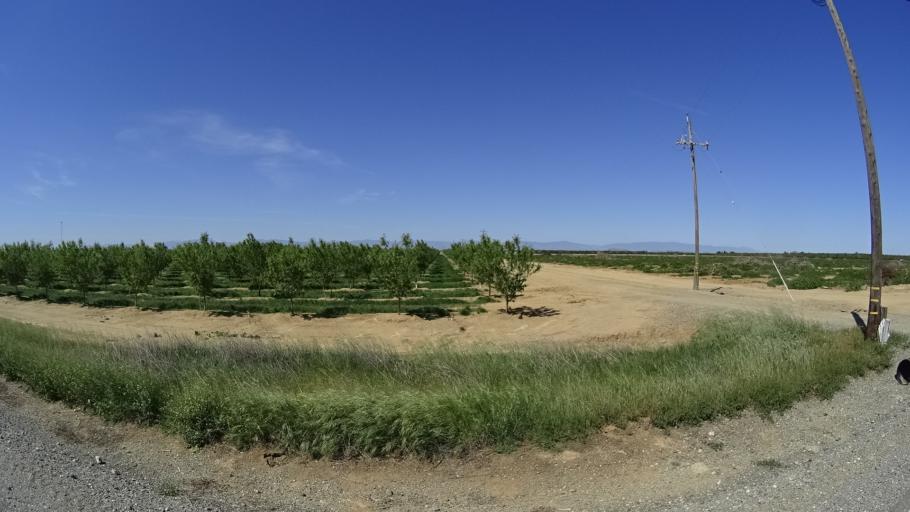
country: US
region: California
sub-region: Glenn County
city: Orland
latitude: 39.6851
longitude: -122.1403
